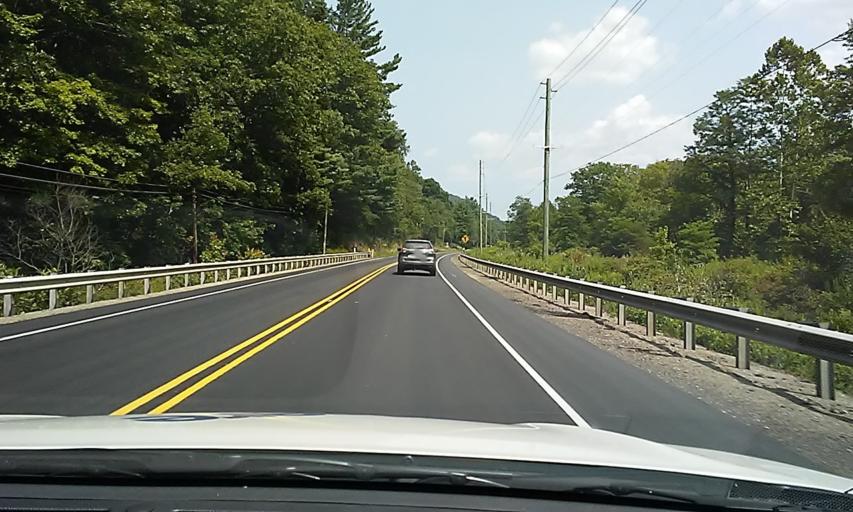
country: US
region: Pennsylvania
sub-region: Cameron County
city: Emporium
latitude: 41.4891
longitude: -78.3022
